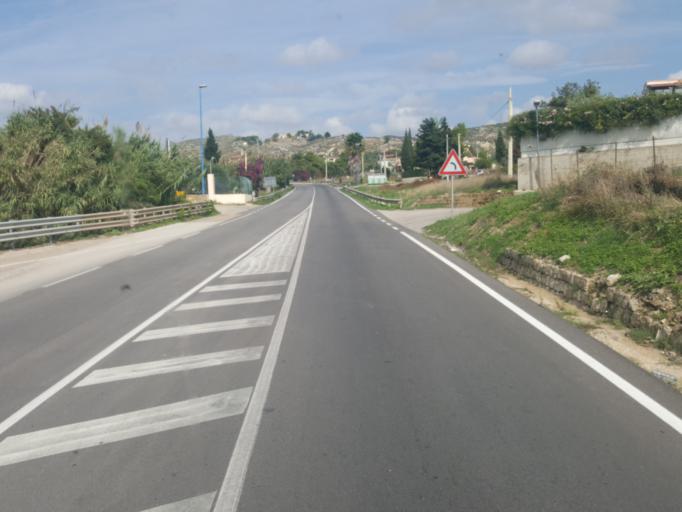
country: IT
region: Sicily
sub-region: Agrigento
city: Porto Empedocle
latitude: 37.2951
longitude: 13.4974
